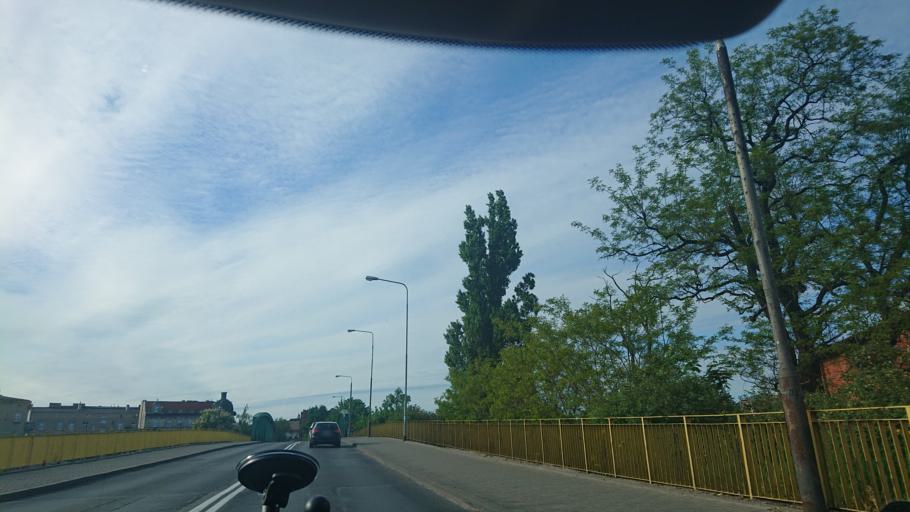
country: PL
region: Greater Poland Voivodeship
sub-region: Powiat gnieznienski
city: Gniezno
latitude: 52.5283
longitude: 17.5971
